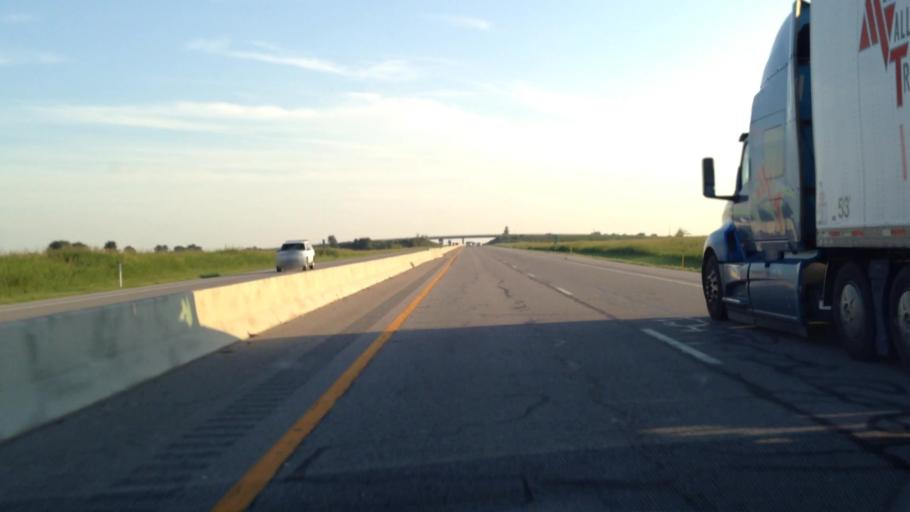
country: US
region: Oklahoma
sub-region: Ottawa County
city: Fairland
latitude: 36.8076
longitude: -94.8772
